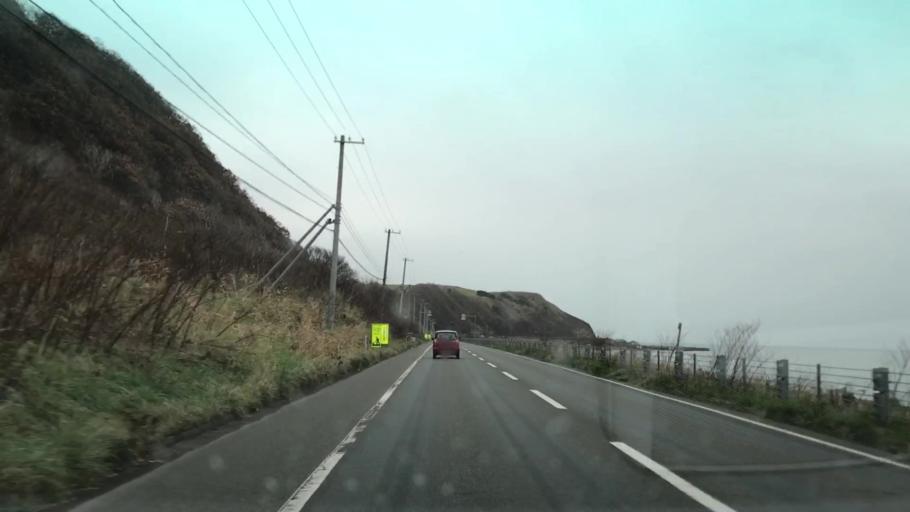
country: JP
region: Hokkaido
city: Shizunai-furukawacho
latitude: 42.3162
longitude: 142.3961
